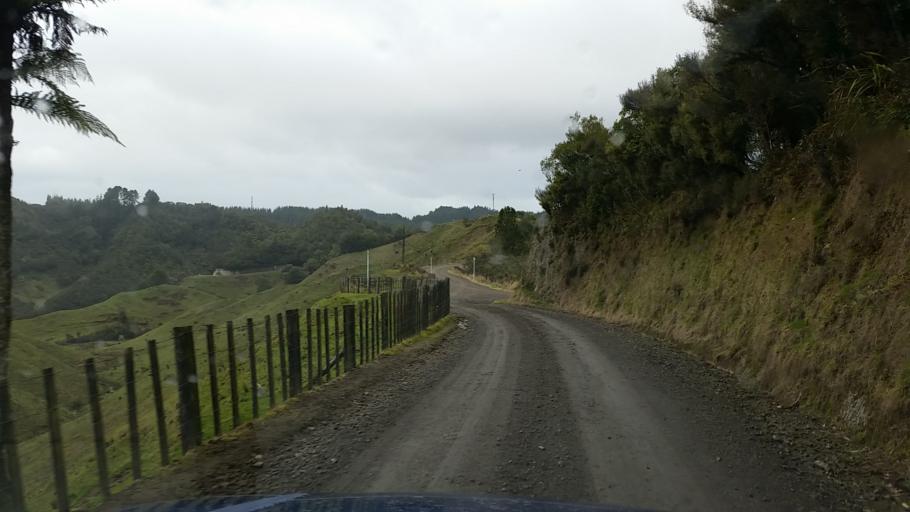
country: NZ
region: Taranaki
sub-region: South Taranaki District
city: Eltham
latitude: -39.1711
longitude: 174.6262
